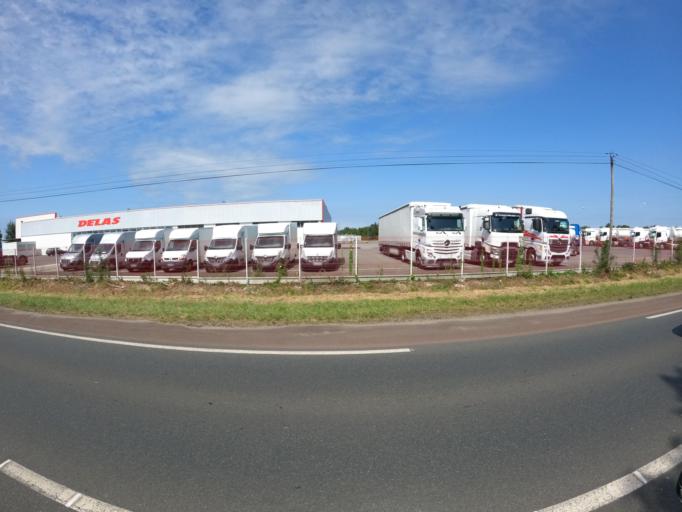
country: FR
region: Poitou-Charentes
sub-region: Departement des Deux-Sevres
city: Bessines
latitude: 46.2877
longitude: -0.5115
